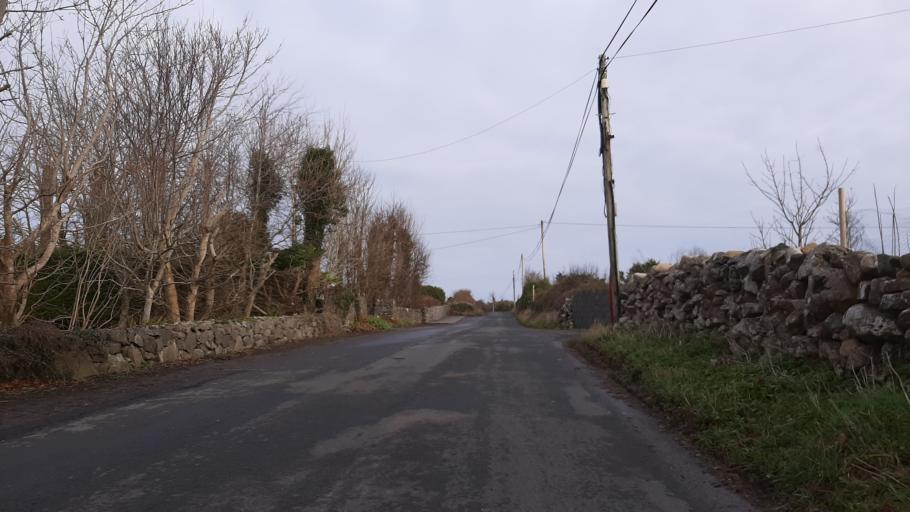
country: IE
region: Connaught
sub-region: County Galway
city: Gaillimh
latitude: 53.3098
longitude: -9.0563
